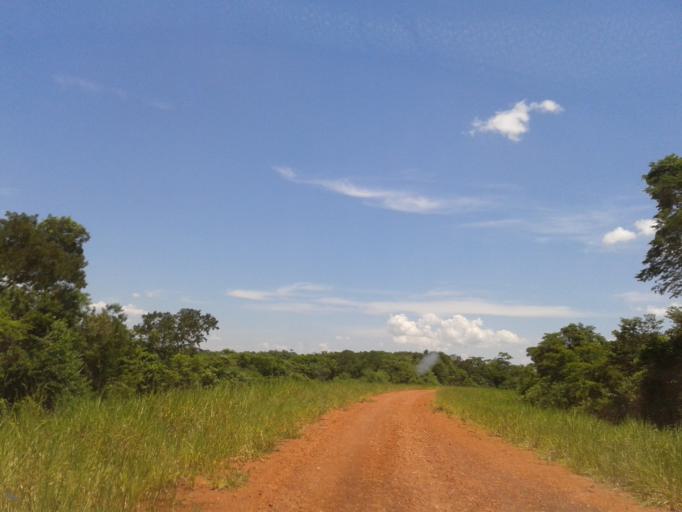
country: BR
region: Minas Gerais
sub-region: Santa Vitoria
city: Santa Vitoria
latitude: -19.1438
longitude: -50.5702
